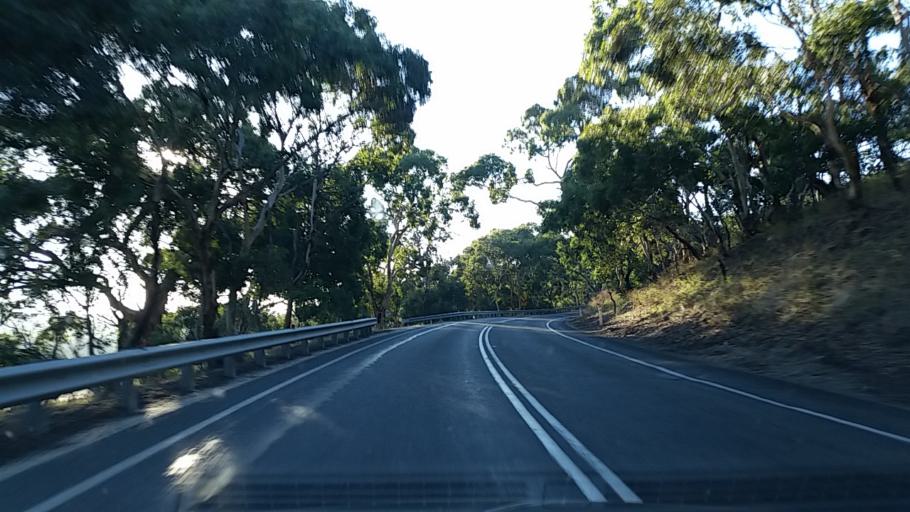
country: AU
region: South Australia
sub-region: Alexandrina
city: Goolwa
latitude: -35.3903
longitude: 138.7514
